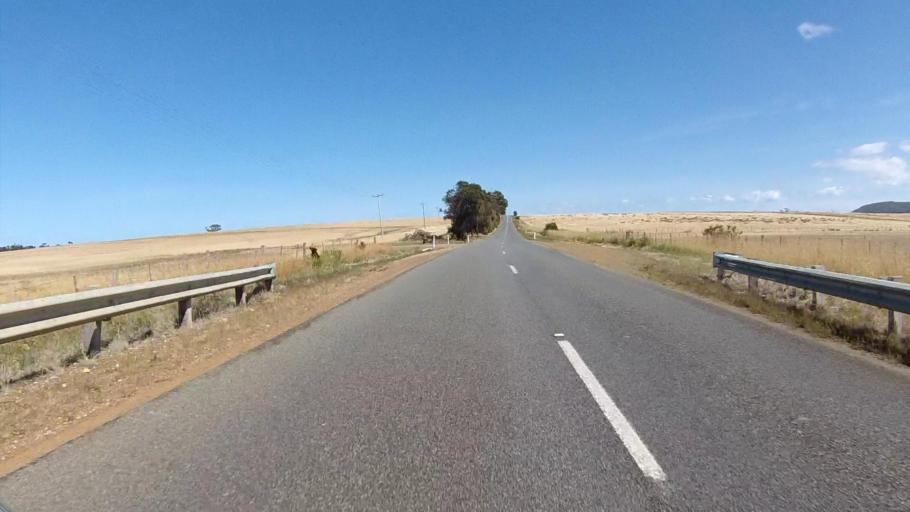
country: AU
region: Tasmania
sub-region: Sorell
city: Sorell
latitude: -42.2469
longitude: 148.0099
